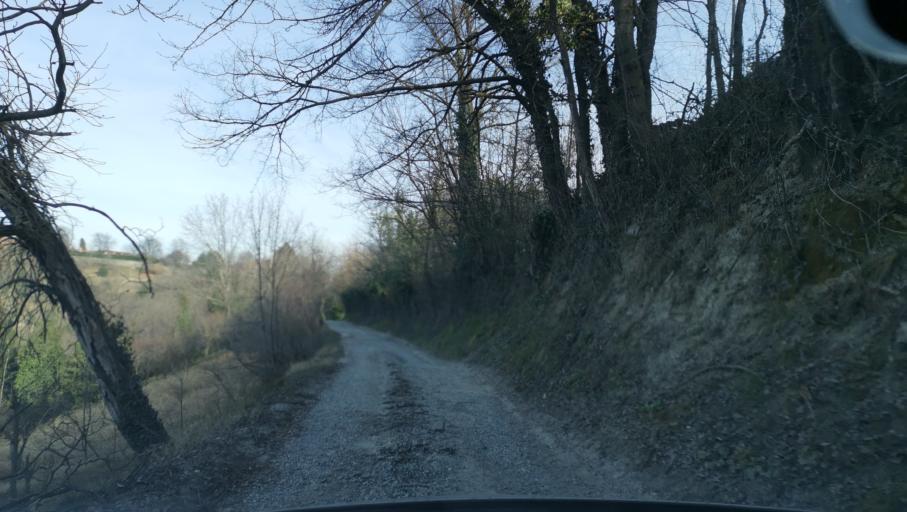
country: IT
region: Piedmont
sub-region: Provincia di Torino
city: Gassino Torinese
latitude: 45.1152
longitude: 7.8278
